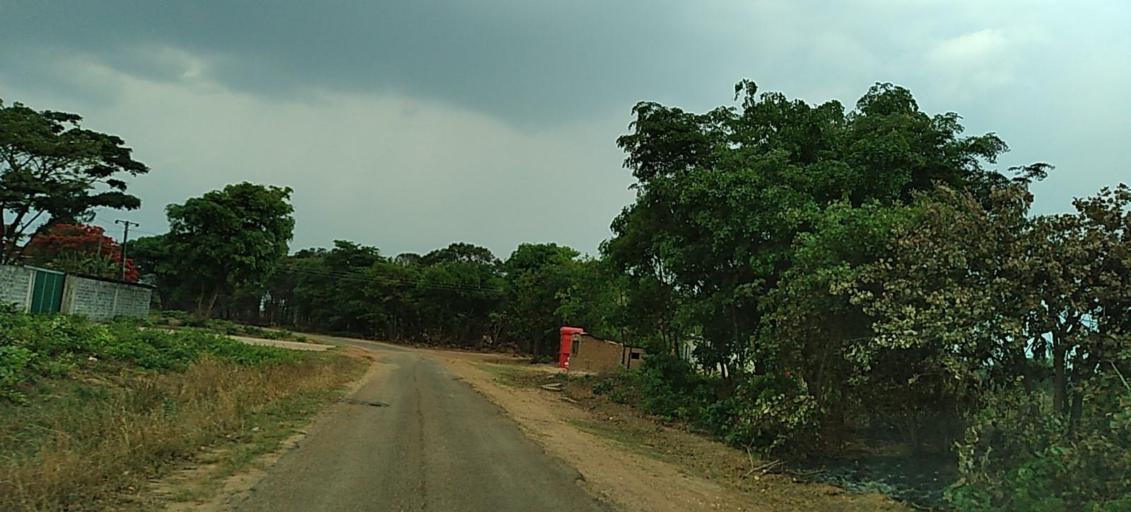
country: ZM
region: Copperbelt
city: Kalulushi
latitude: -12.8908
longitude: 28.1246
